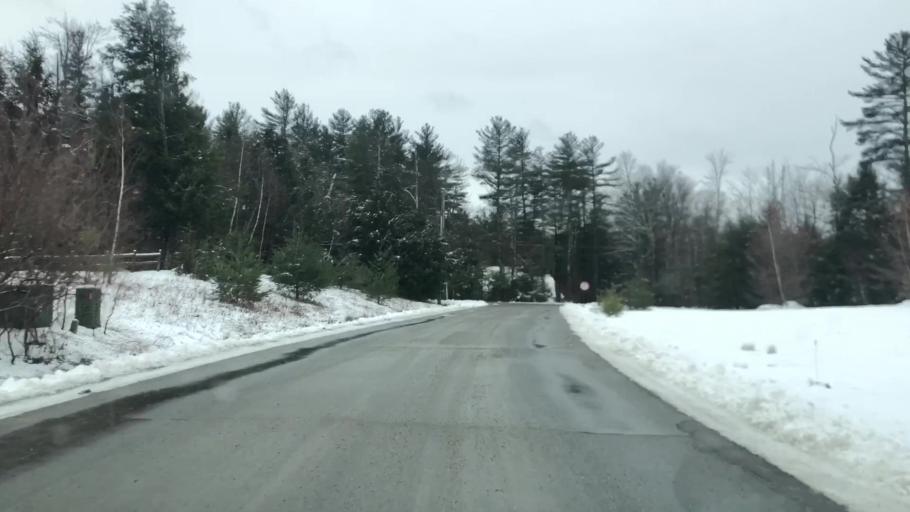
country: US
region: New Hampshire
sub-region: Hillsborough County
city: New Boston
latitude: 42.9940
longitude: -71.6485
